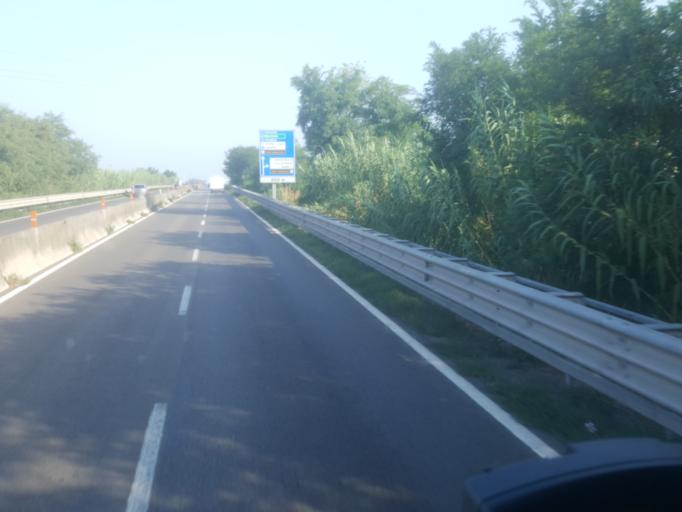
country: IT
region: Emilia-Romagna
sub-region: Provincia di Ravenna
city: Madonna Dell'Albero
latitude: 44.3912
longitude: 12.1865
